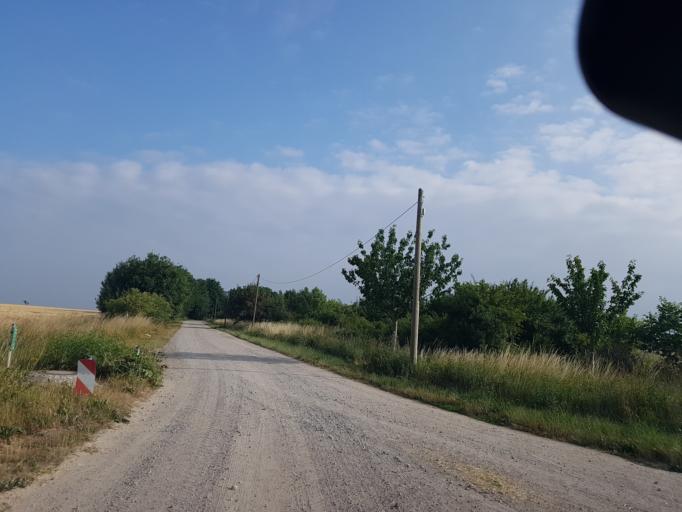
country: DE
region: Saxony-Anhalt
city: Kropstadt
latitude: 52.0052
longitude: 12.8197
